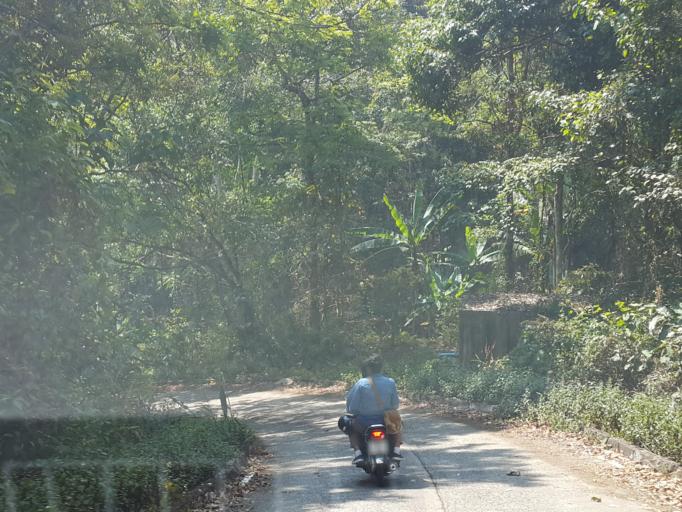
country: TH
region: Chiang Mai
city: Mae On
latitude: 18.8420
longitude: 99.3746
